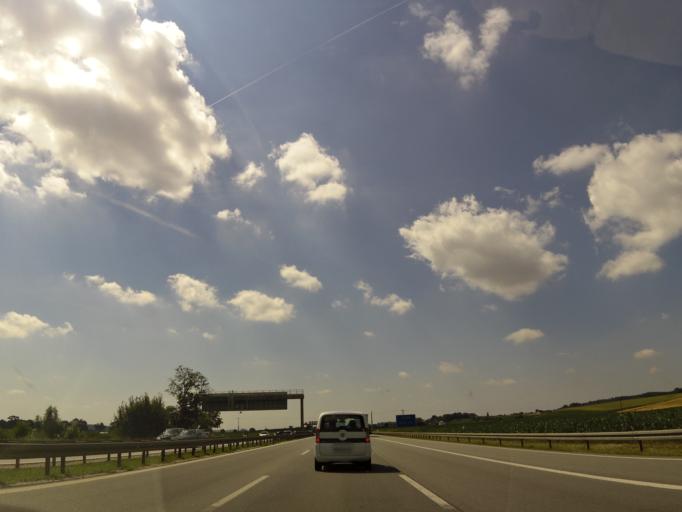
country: DE
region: Bavaria
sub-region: Upper Bavaria
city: Allershausen
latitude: 48.4212
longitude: 11.5897
